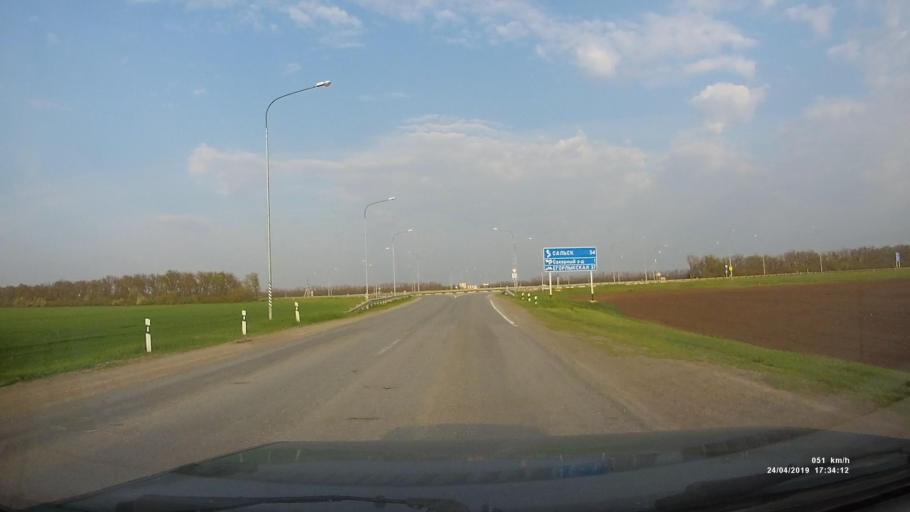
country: RU
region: Rostov
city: Tselina
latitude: 46.5266
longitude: 41.0788
